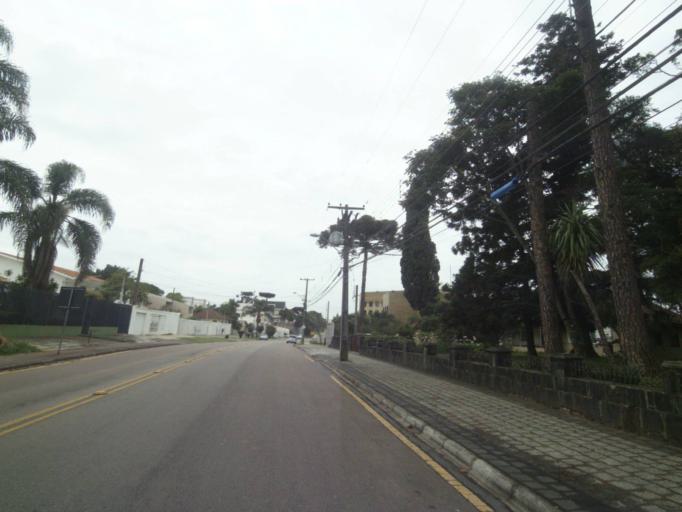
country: BR
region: Parana
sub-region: Curitiba
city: Curitiba
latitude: -25.4088
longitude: -49.2969
